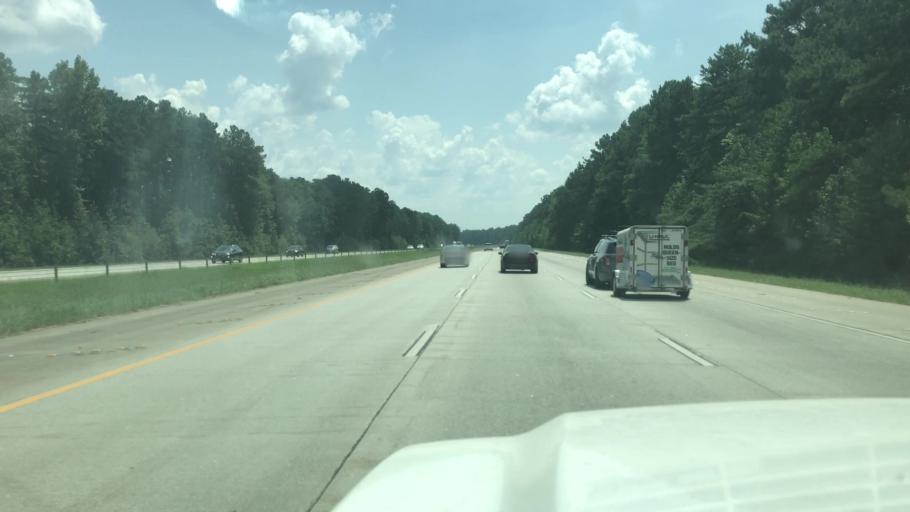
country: US
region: Georgia
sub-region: Coweta County
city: Grantville
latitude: 33.2767
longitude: -84.8014
